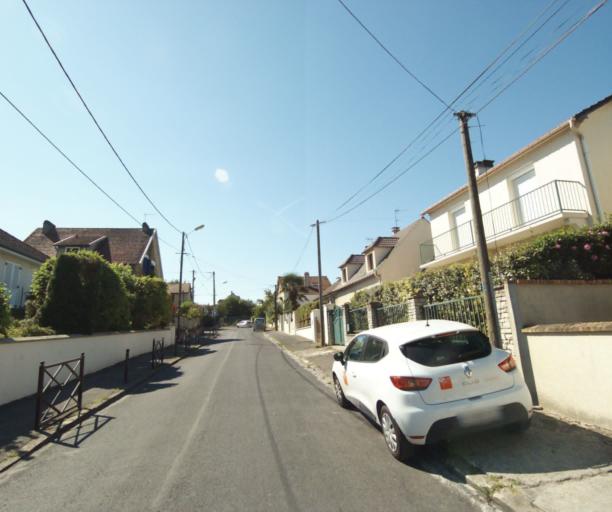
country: FR
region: Ile-de-France
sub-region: Departement de Seine-et-Marne
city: Lagny-sur-Marne
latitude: 48.8731
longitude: 2.7104
